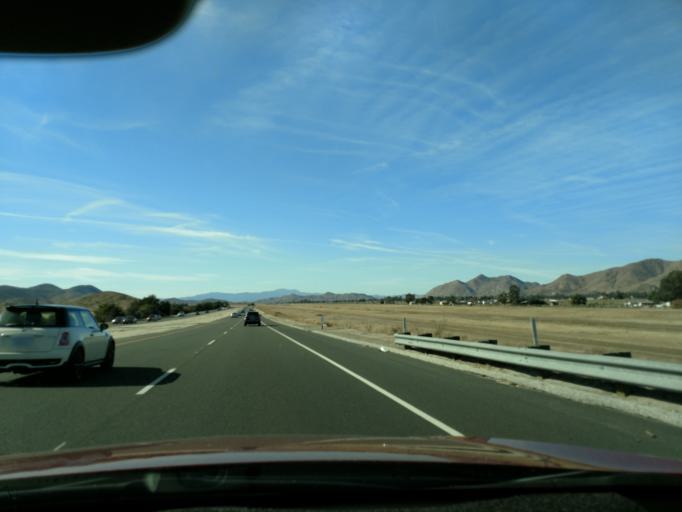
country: US
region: California
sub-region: Riverside County
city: Winchester
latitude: 33.6985
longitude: -117.0510
